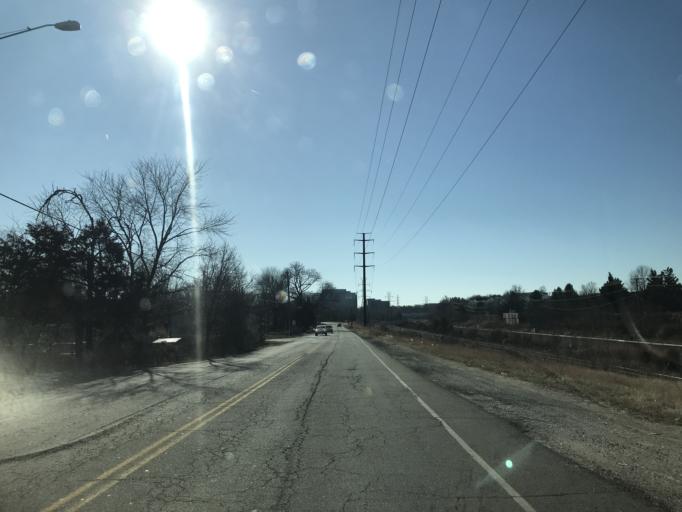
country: US
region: Virginia
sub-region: Fairfax County
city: Franconia
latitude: 38.7790
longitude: -77.1564
